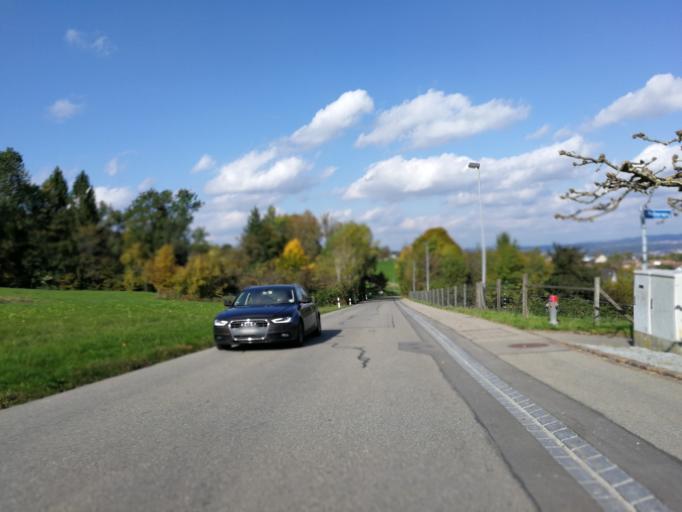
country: CH
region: Zurich
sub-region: Bezirk Uster
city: Egg
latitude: 47.2991
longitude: 8.6827
